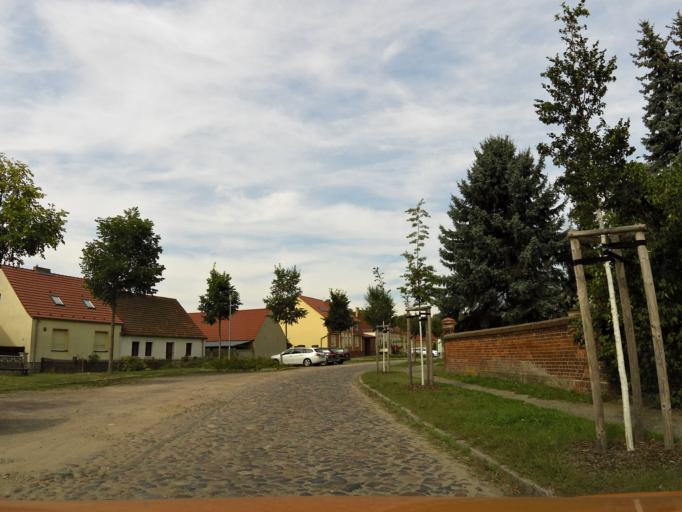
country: DE
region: Brandenburg
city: Michendorf
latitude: 52.2445
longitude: 13.0804
